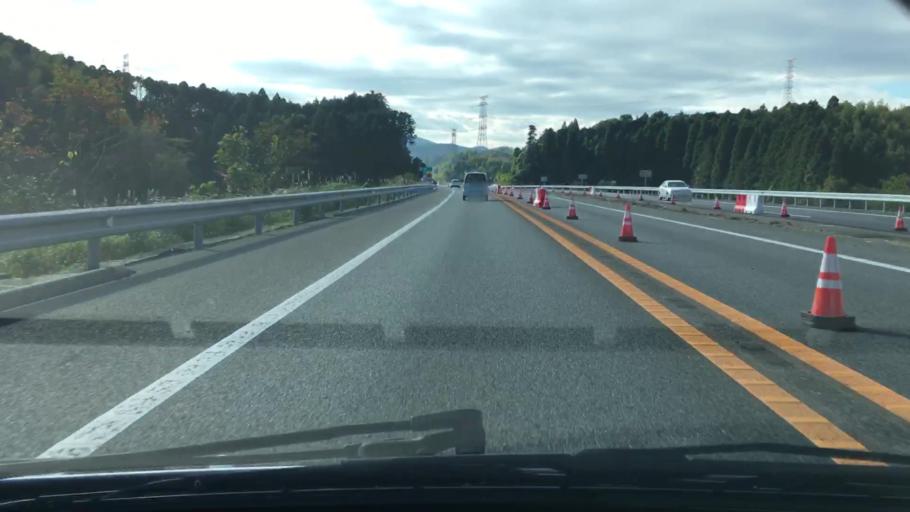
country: JP
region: Chiba
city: Kimitsu
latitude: 35.2907
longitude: 139.9302
